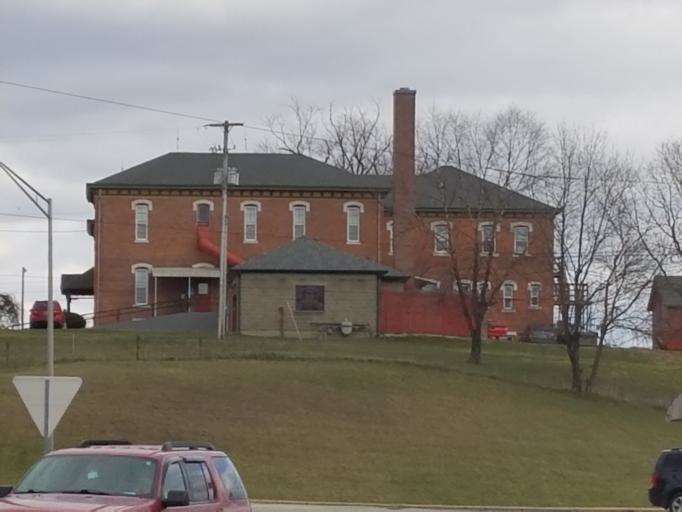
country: US
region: Indiana
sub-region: Hendricks County
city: Danville
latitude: 39.7578
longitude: -86.5072
